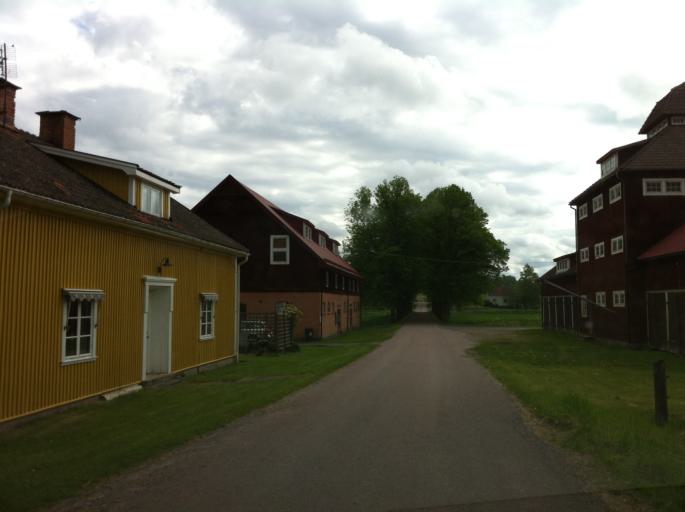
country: SE
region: Vaermland
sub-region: Sunne Kommun
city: Sunne
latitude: 59.9020
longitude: 13.1670
